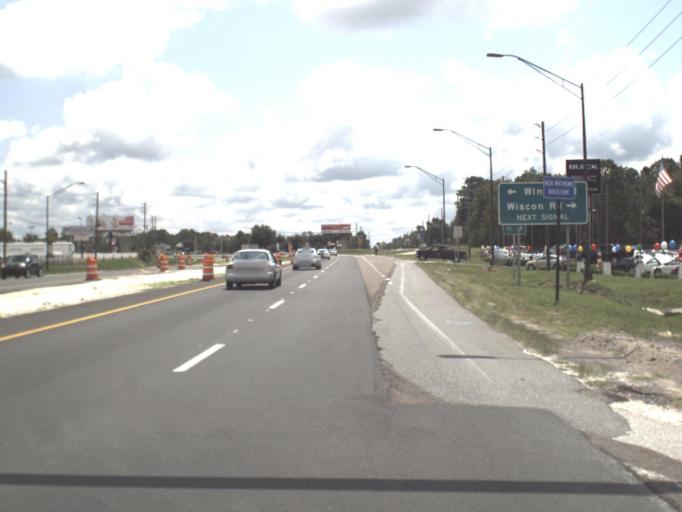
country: US
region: Florida
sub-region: Hernando County
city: Brookridge
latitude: 28.5338
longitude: -82.4785
